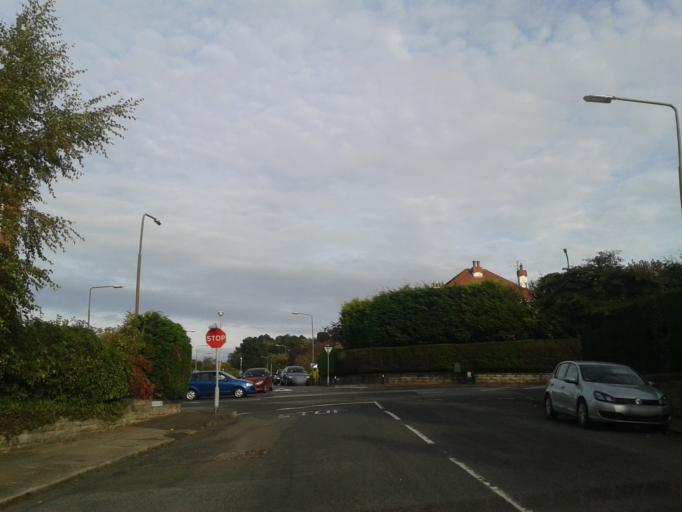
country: GB
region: Scotland
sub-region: Edinburgh
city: Edinburgh
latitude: 55.9159
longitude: -3.2119
